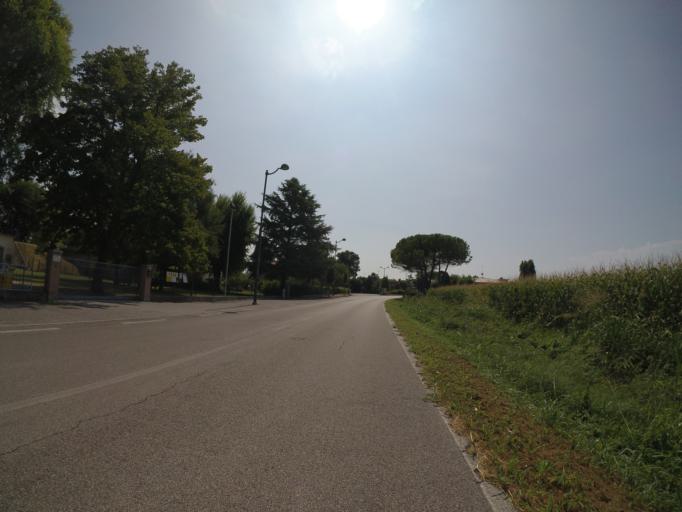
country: IT
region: Veneto
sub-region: Provincia di Venezia
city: Bibione
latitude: 45.6682
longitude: 13.0596
